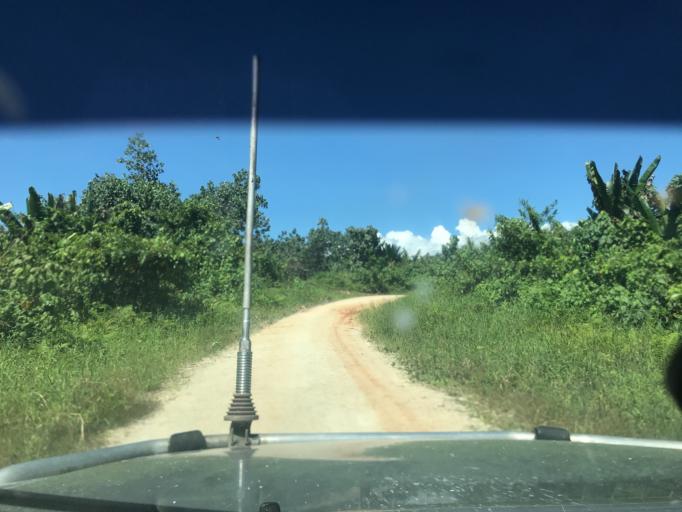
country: SB
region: Malaita
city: Auki
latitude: -8.7288
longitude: 160.9008
